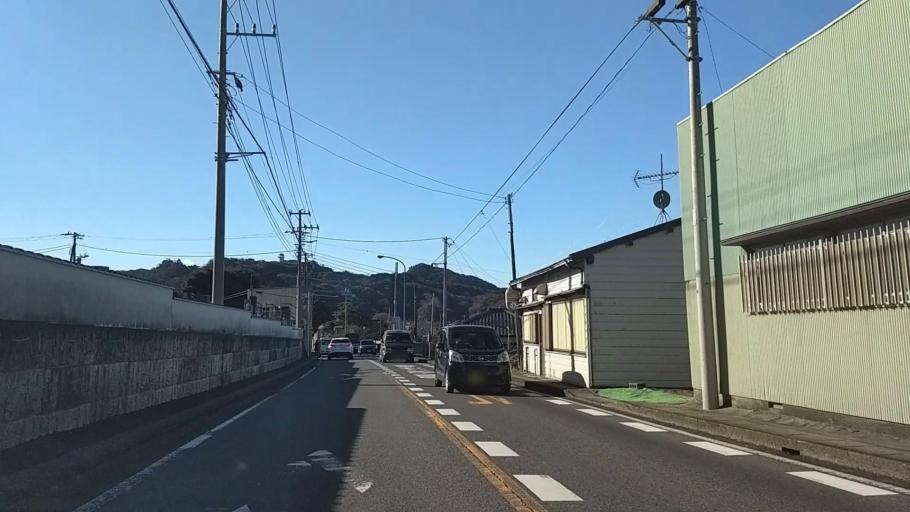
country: JP
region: Chiba
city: Futtsu
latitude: 35.2097
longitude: 139.8467
